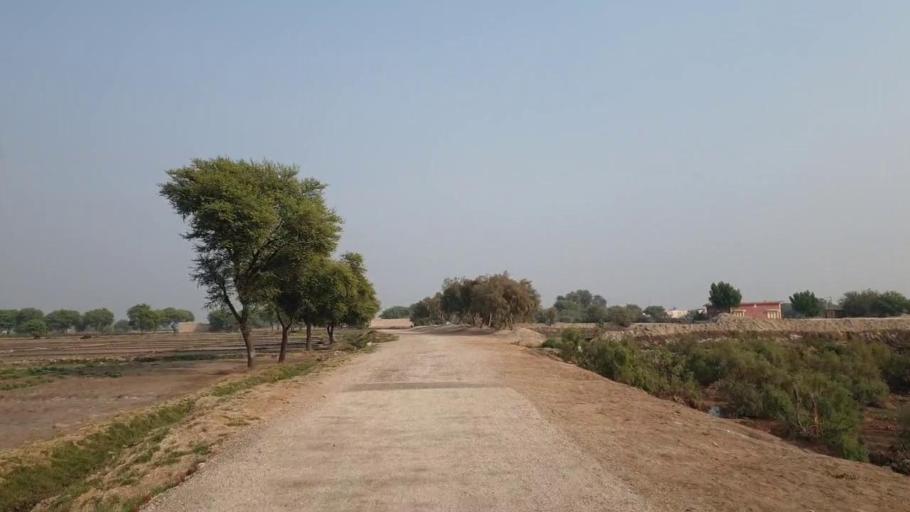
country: PK
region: Sindh
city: Bhan
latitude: 26.4583
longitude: 67.7266
